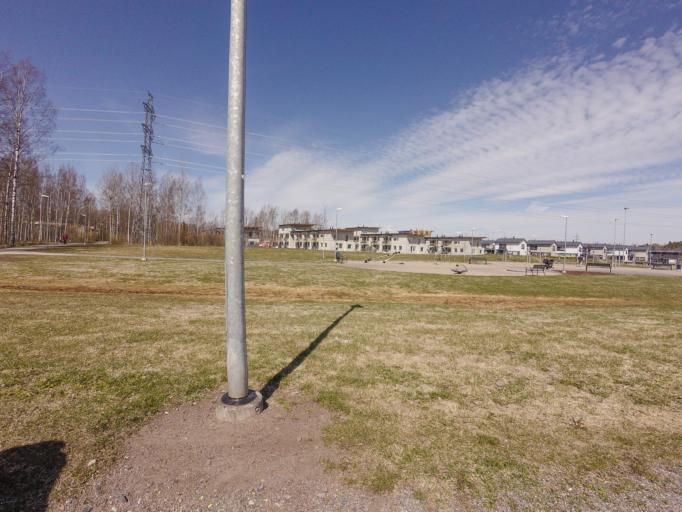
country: FI
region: Uusimaa
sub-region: Helsinki
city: Vantaa
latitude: 60.2295
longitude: 25.1062
